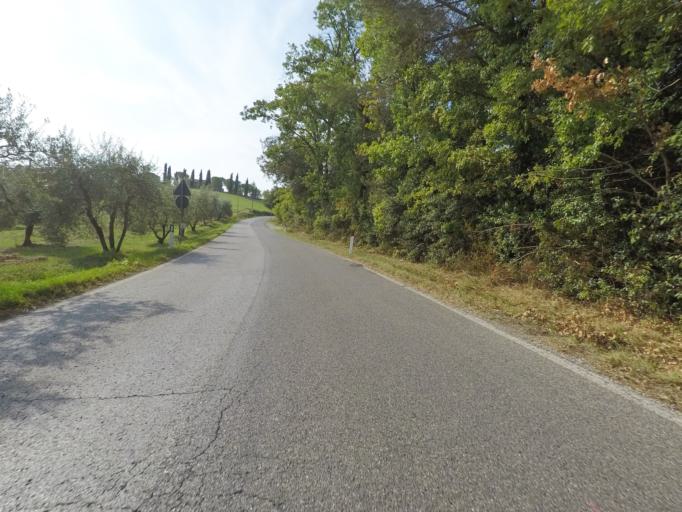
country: IT
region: Tuscany
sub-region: Provincia di Siena
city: Belverde
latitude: 43.3970
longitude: 11.3495
